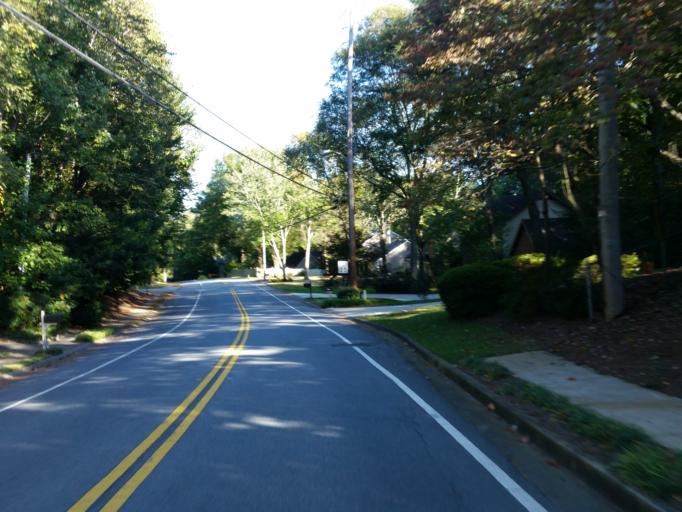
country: US
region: Georgia
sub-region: Fulton County
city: Roswell
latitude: 33.9925
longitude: -84.3956
